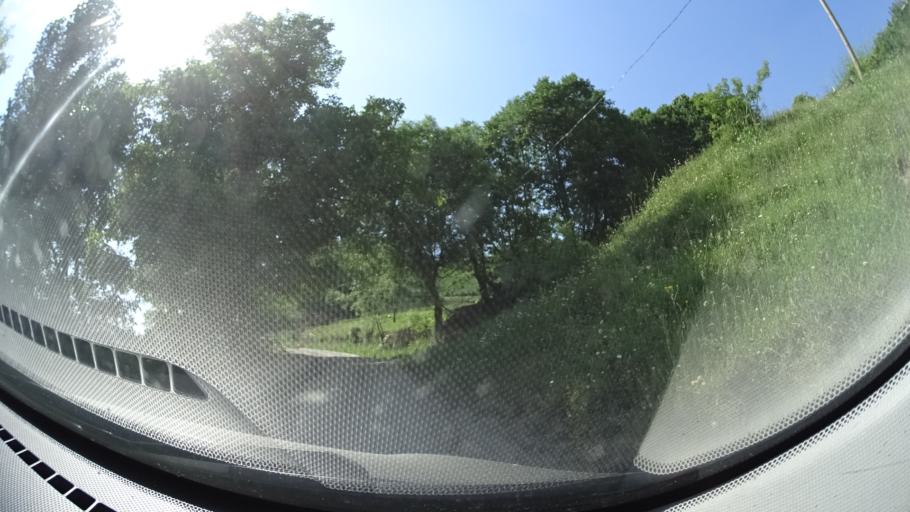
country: GE
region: Ajaria
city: Dioknisi
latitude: 41.6451
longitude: 42.4637
